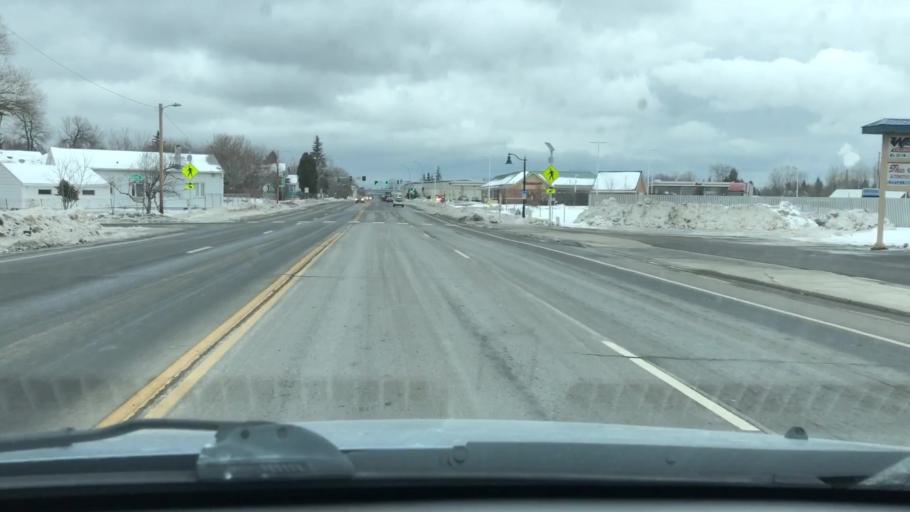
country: US
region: Minnesota
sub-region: Saint Louis County
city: Proctor
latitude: 46.7298
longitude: -92.1823
